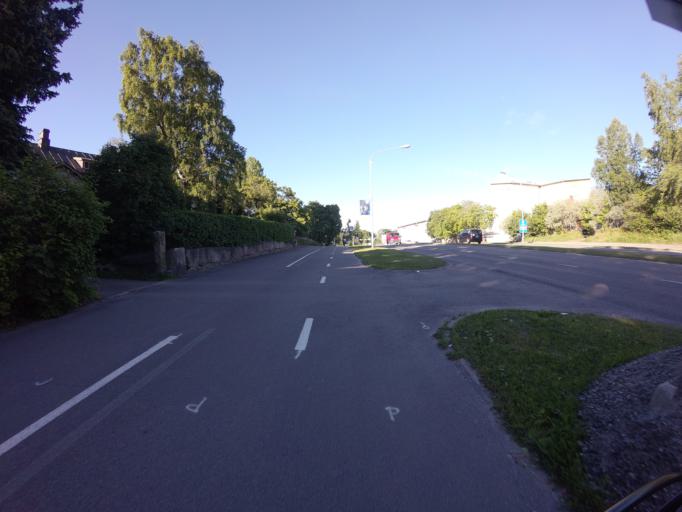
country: FI
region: Varsinais-Suomi
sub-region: Turku
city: Turku
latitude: 60.4621
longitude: 22.2691
